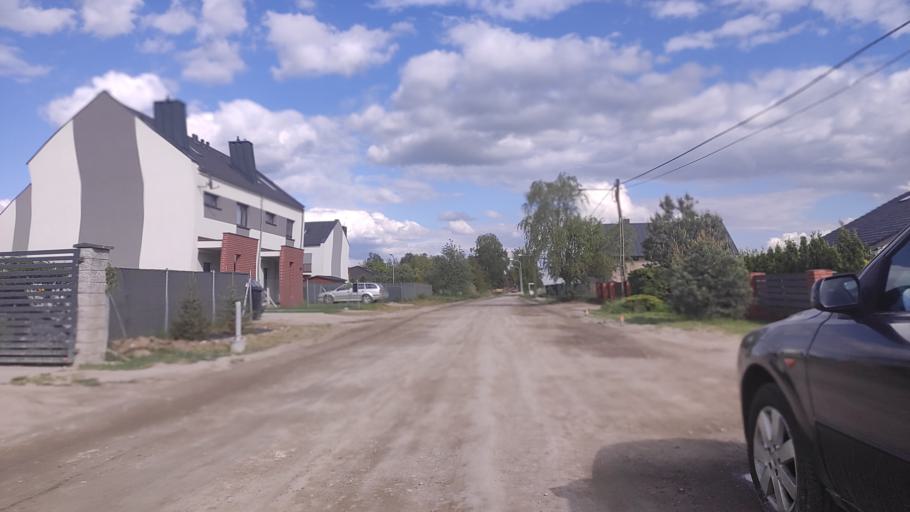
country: PL
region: Greater Poland Voivodeship
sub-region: Powiat poznanski
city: Swarzedz
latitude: 52.3896
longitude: 17.1229
